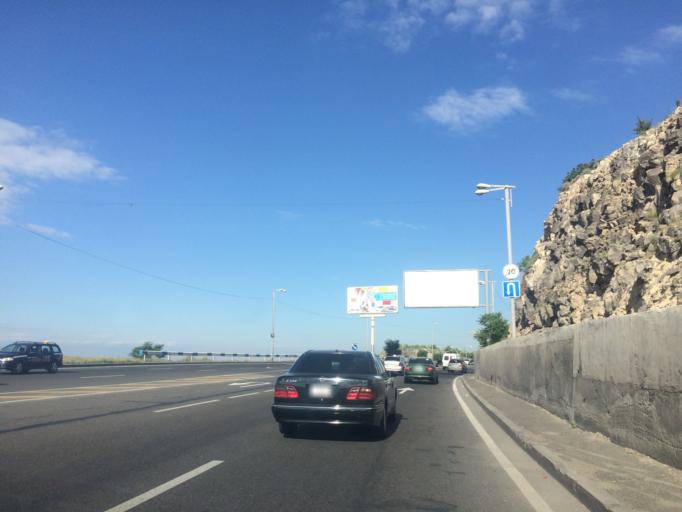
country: AM
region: Yerevan
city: Yerevan
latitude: 40.1937
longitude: 44.5223
